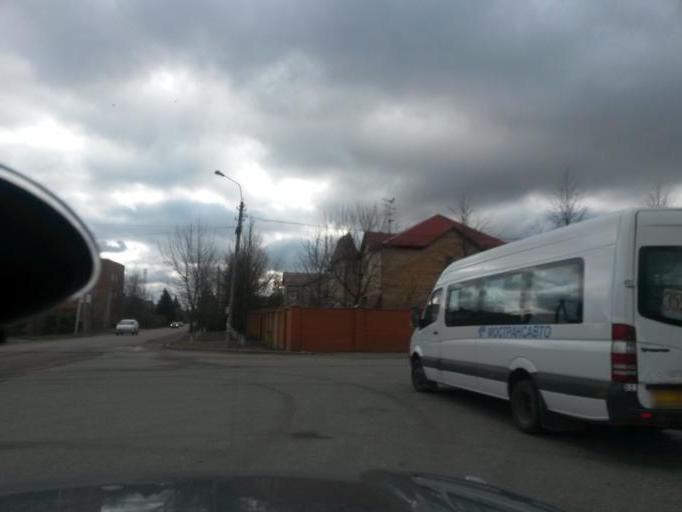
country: RU
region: Moskovskaya
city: Alekseyevka
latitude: 55.6020
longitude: 37.8184
